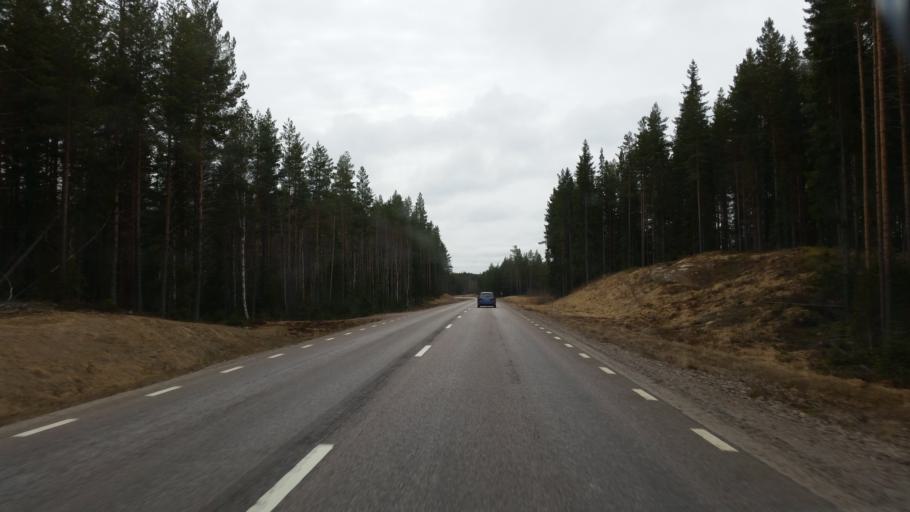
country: SE
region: Gaevleborg
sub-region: Ovanakers Kommun
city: Edsbyn
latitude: 61.1823
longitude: 15.8784
